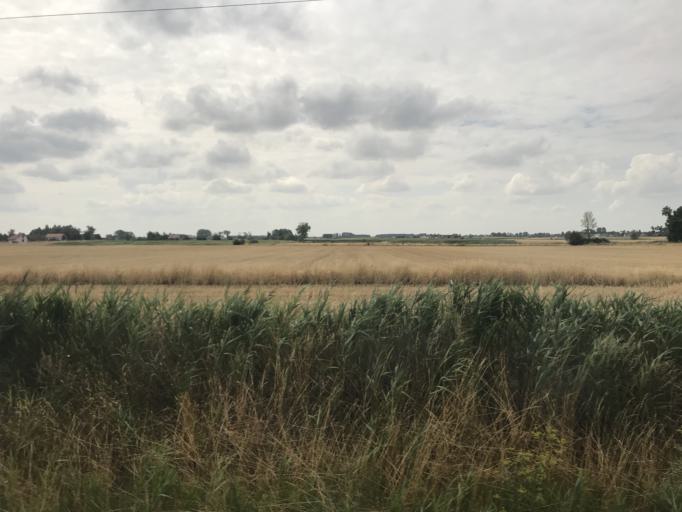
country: PL
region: Greater Poland Voivodeship
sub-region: Powiat gnieznienski
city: Niechanowo
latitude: 52.5342
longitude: 17.6801
